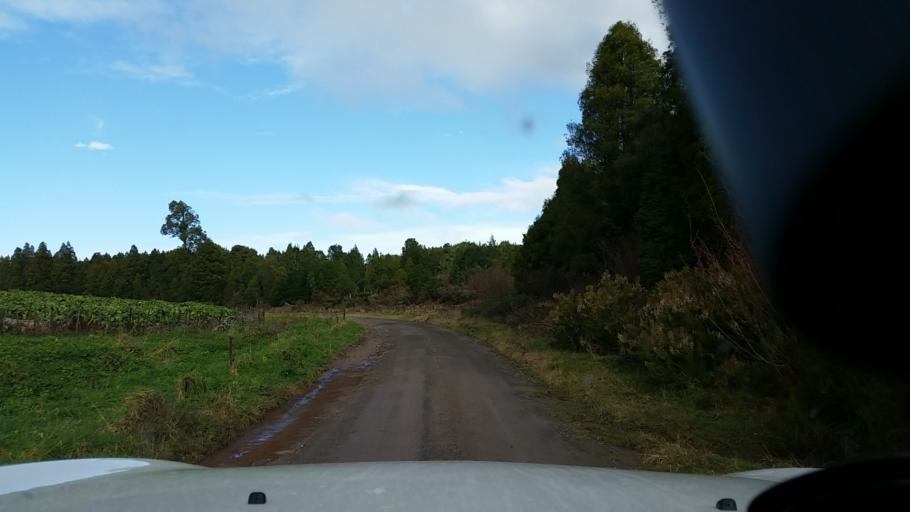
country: NZ
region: Bay of Plenty
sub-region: Rotorua District
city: Rotorua
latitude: -38.0765
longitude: 176.0363
